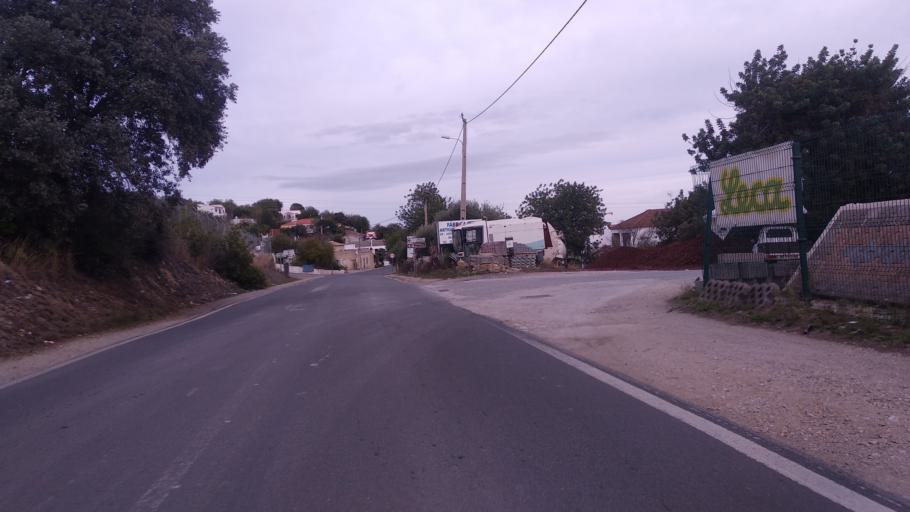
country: PT
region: Faro
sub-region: Sao Bras de Alportel
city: Sao Bras de Alportel
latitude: 37.1530
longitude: -7.9031
